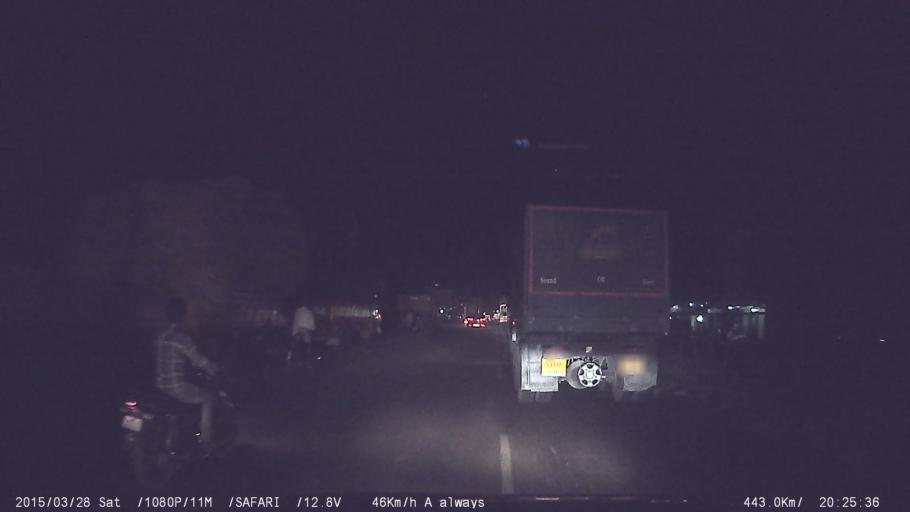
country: IN
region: Karnataka
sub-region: Mandya
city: Maddur
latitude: 12.5999
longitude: 77.0528
